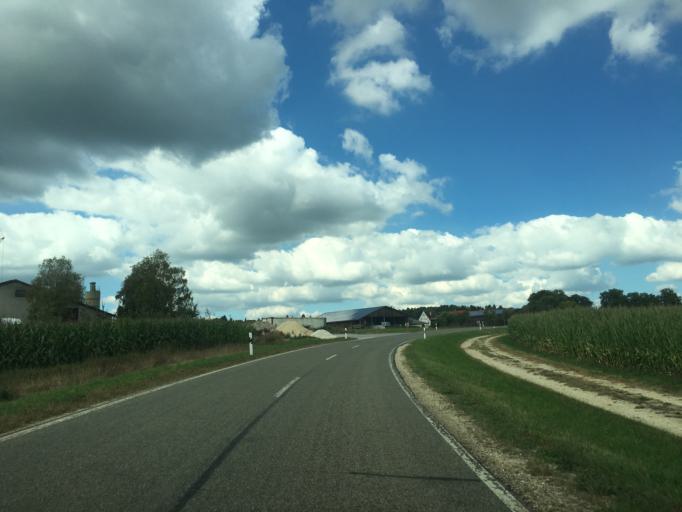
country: DE
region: Baden-Wuerttemberg
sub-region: Tuebingen Region
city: Hayingen
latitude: 48.2717
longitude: 9.4826
